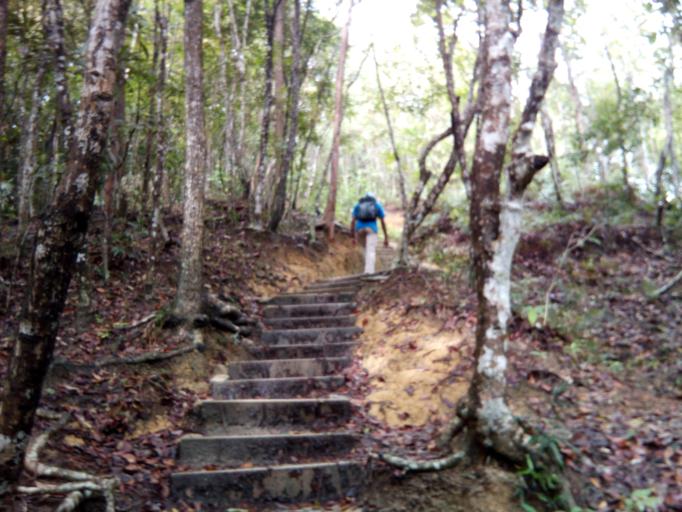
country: MY
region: Penang
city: Tanjung Tokong
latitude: 5.4326
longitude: 100.2923
